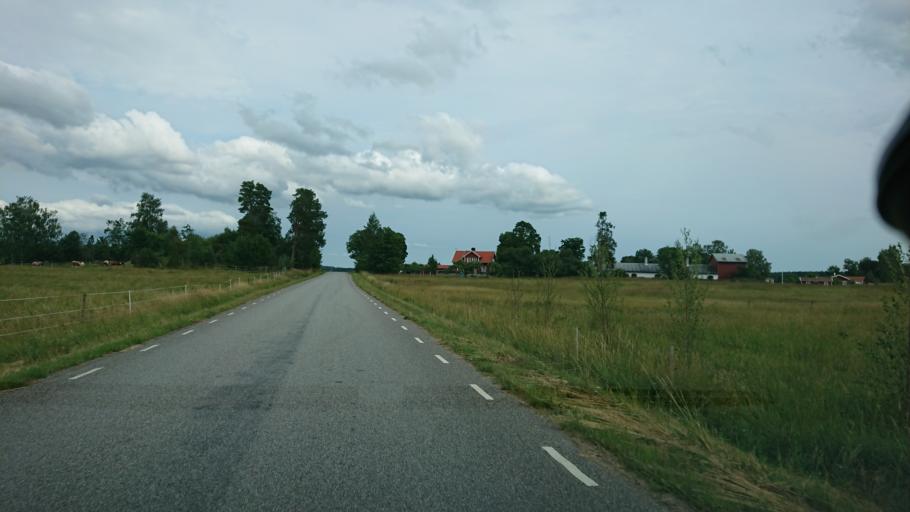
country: SE
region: Uppsala
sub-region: Osthammars Kommun
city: Bjorklinge
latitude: 59.9986
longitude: 17.4843
